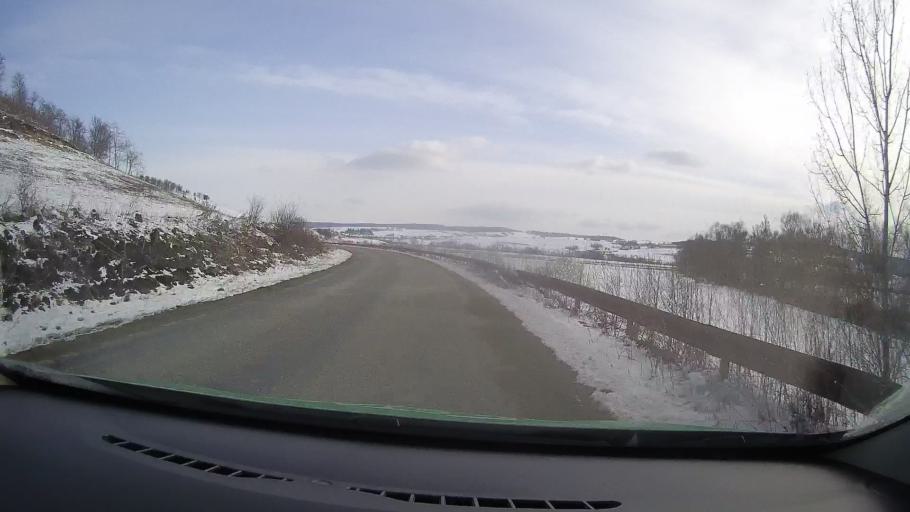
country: RO
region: Sibiu
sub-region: Comuna Merghindeal
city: Merghindeal
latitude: 45.9794
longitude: 24.7007
